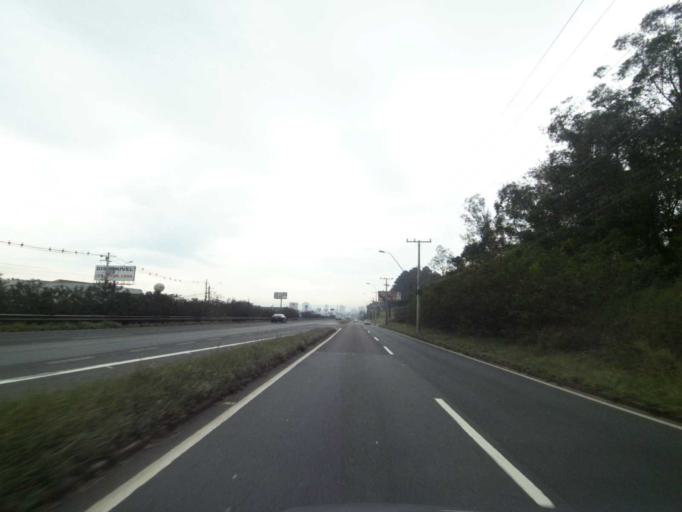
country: BR
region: Rio Grande do Sul
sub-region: Sao Leopoldo
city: Sao Leopoldo
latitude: -29.7838
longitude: -51.1616
